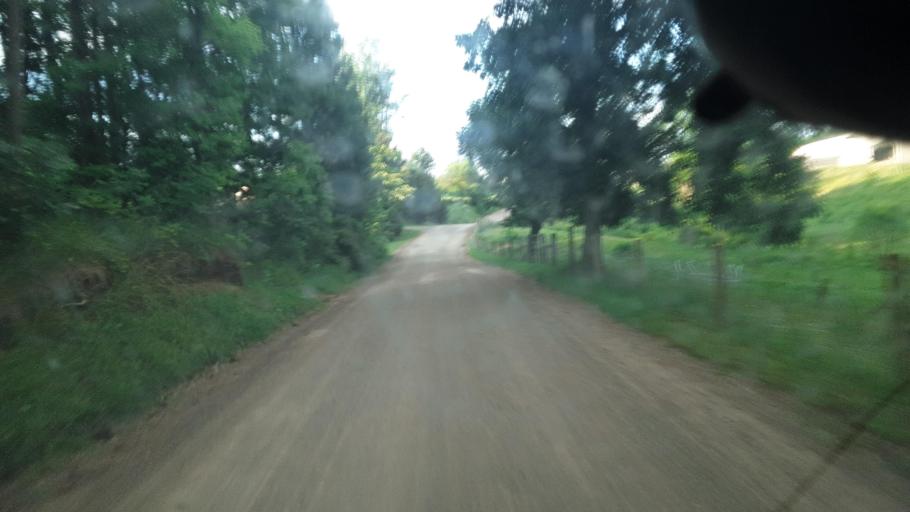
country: US
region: Ohio
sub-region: Holmes County
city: Millersburg
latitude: 40.4324
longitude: -81.8477
